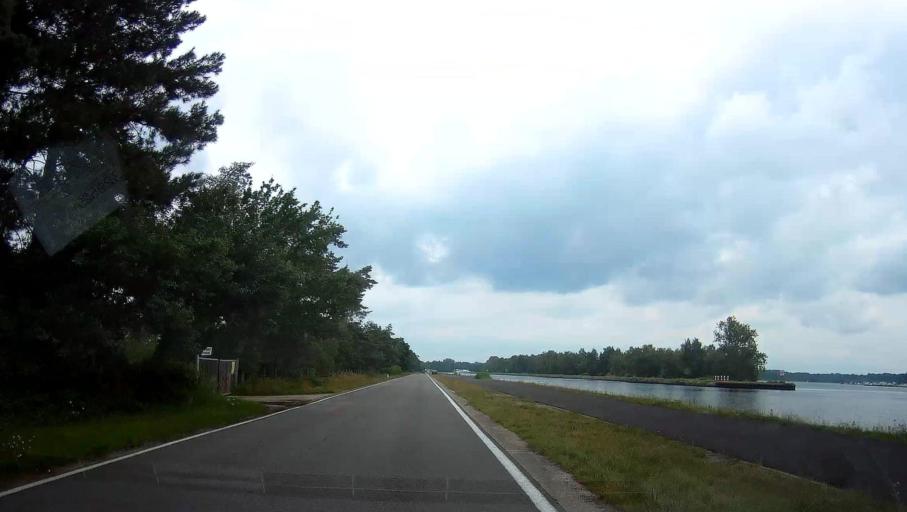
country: BE
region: Flanders
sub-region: Provincie Antwerpen
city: Dessel
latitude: 51.2233
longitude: 5.1620
